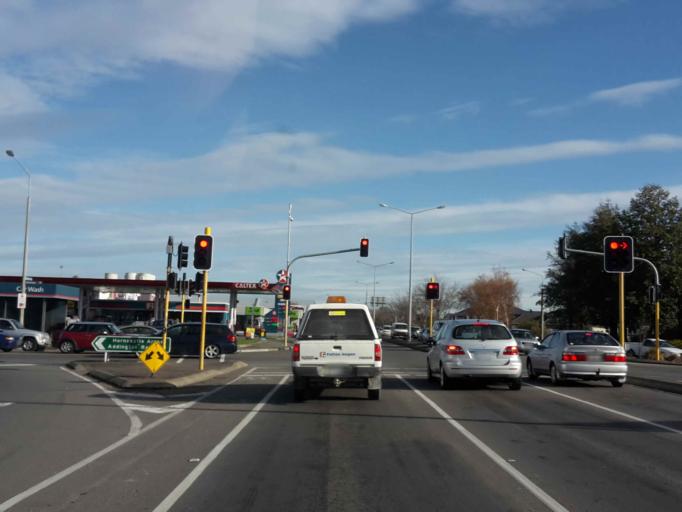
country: NZ
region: Canterbury
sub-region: Christchurch City
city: Christchurch
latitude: -43.5375
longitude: 172.5970
